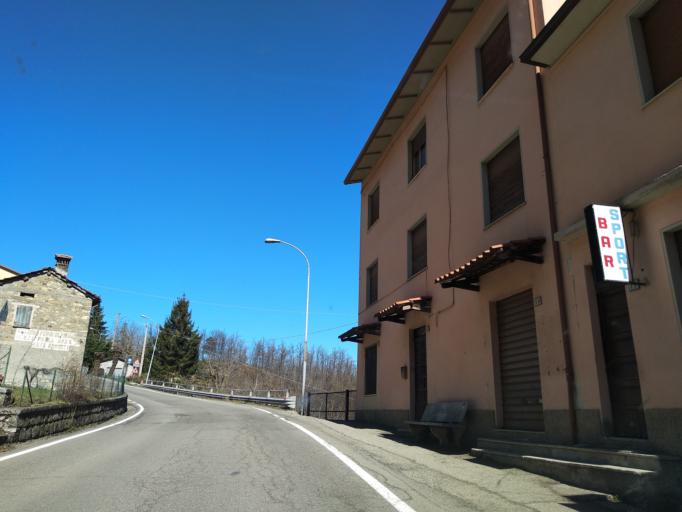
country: IT
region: Emilia-Romagna
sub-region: Provincia di Reggio Emilia
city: Ramiseto
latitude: 44.4147
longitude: 10.2986
